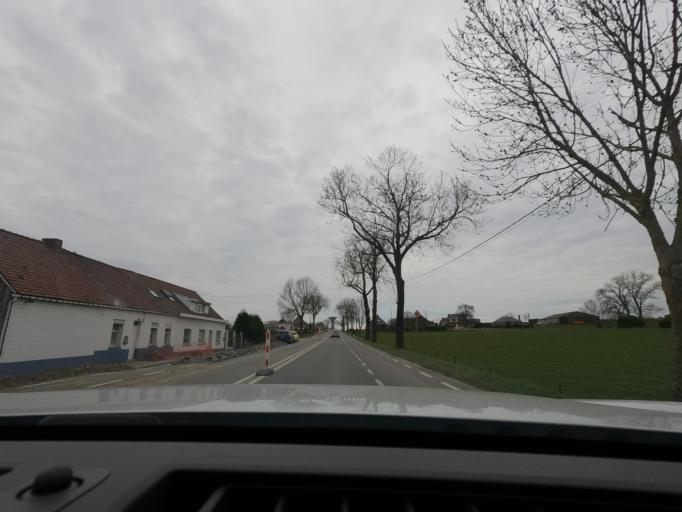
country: BE
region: Wallonia
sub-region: Province du Hainaut
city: Silly
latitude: 50.6616
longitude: 3.8732
